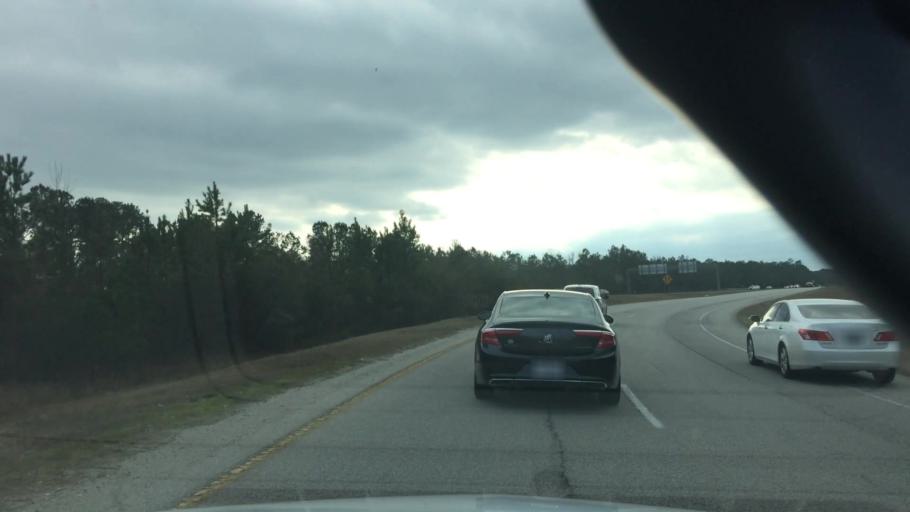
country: US
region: South Carolina
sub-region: Horry County
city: North Myrtle Beach
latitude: 33.8748
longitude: -78.6838
